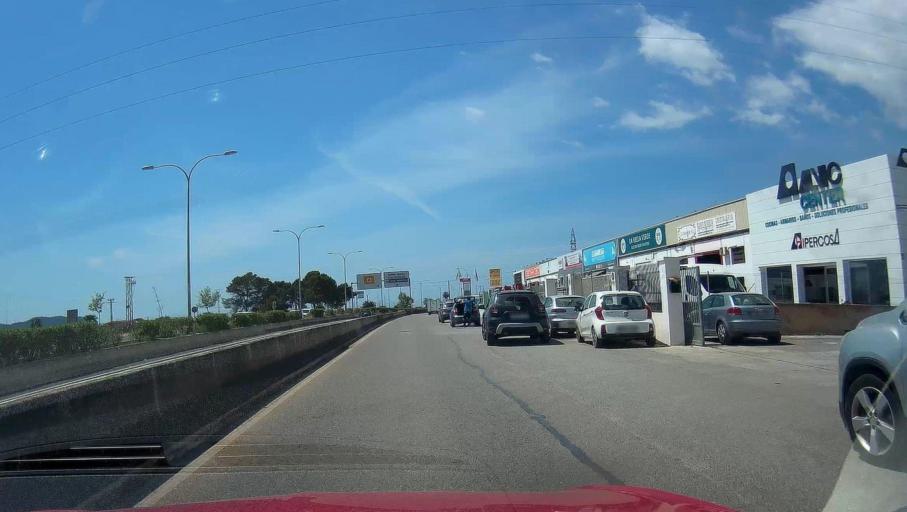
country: ES
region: Balearic Islands
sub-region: Illes Balears
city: Ibiza
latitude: 38.8845
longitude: 1.3898
